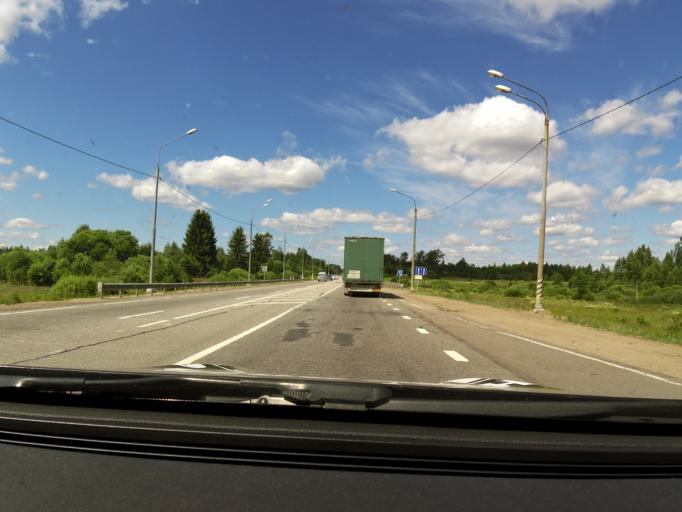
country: RU
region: Tverskaya
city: Kuzhenkino
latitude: 57.7847
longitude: 33.9017
